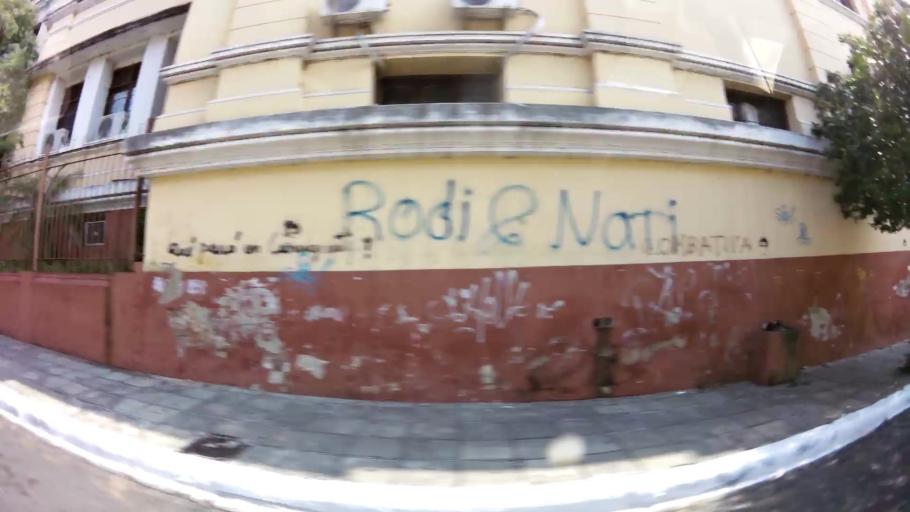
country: PY
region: Asuncion
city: Asuncion
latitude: -25.2829
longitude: -57.6320
